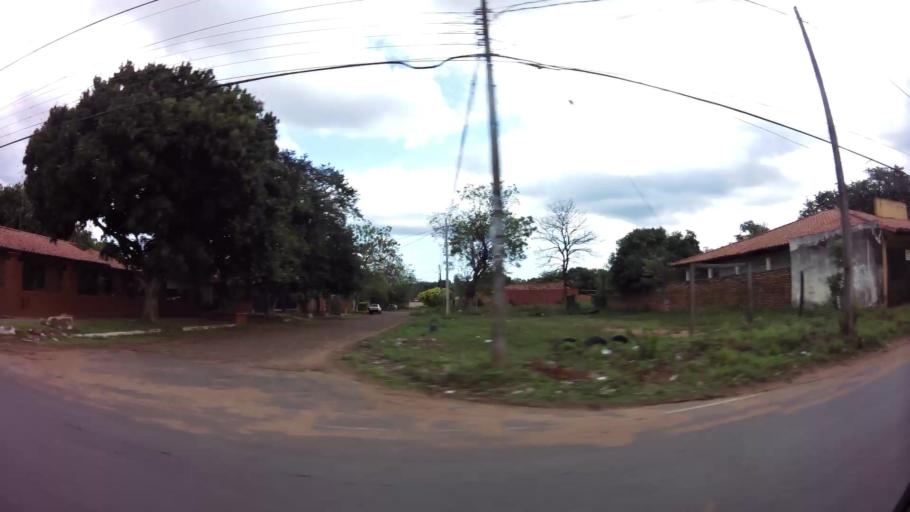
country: PY
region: Central
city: San Lorenzo
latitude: -25.2885
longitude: -57.5053
